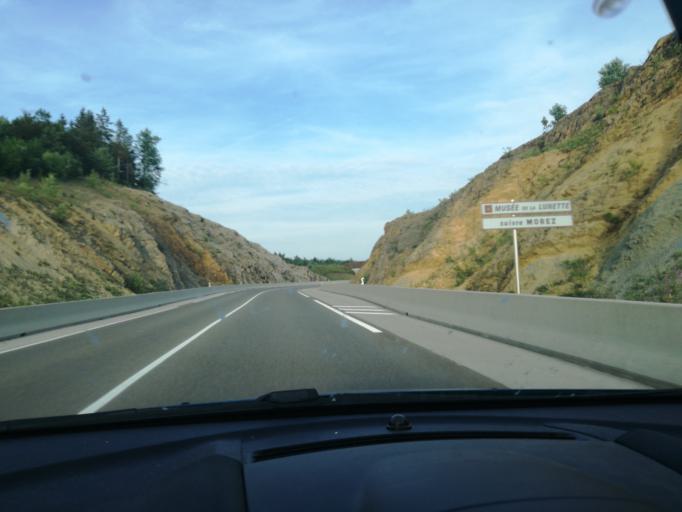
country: FR
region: Franche-Comte
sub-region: Departement du Jura
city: Morbier
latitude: 46.5830
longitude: 5.9559
